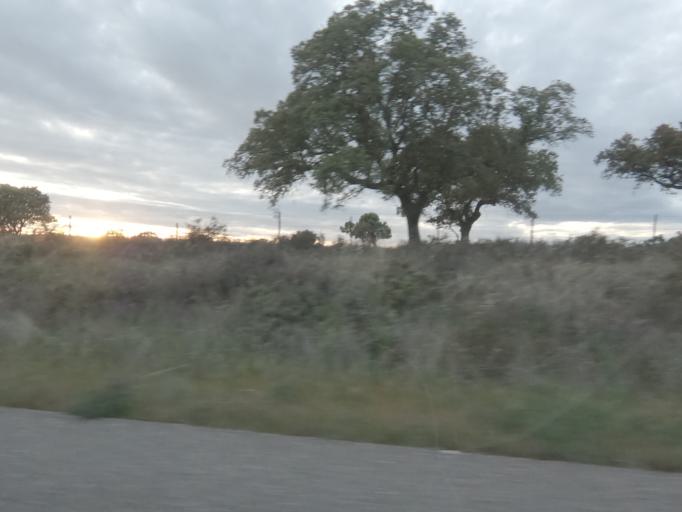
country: ES
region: Extremadura
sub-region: Provincia de Badajoz
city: La Roca de la Sierra
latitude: 39.0706
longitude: -6.7560
